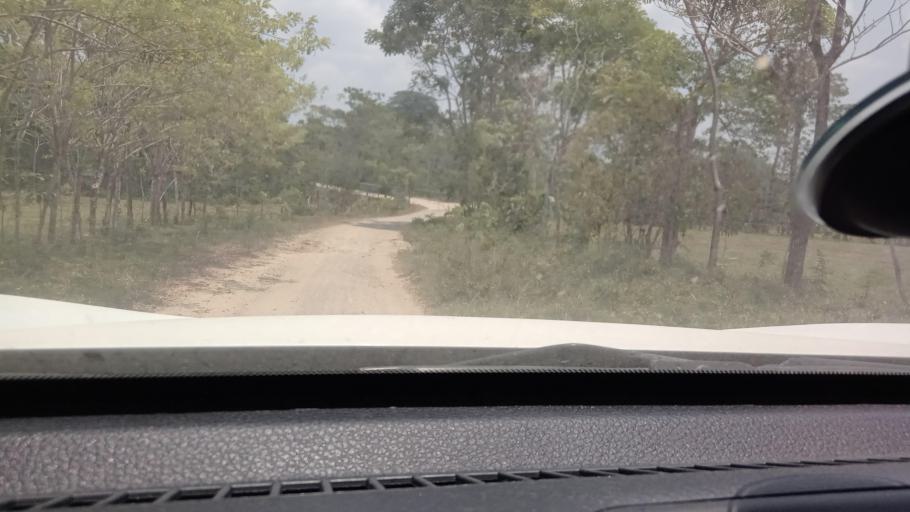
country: MX
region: Tabasco
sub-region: Huimanguillo
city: Francisco Rueda
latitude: 17.4958
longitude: -93.9092
